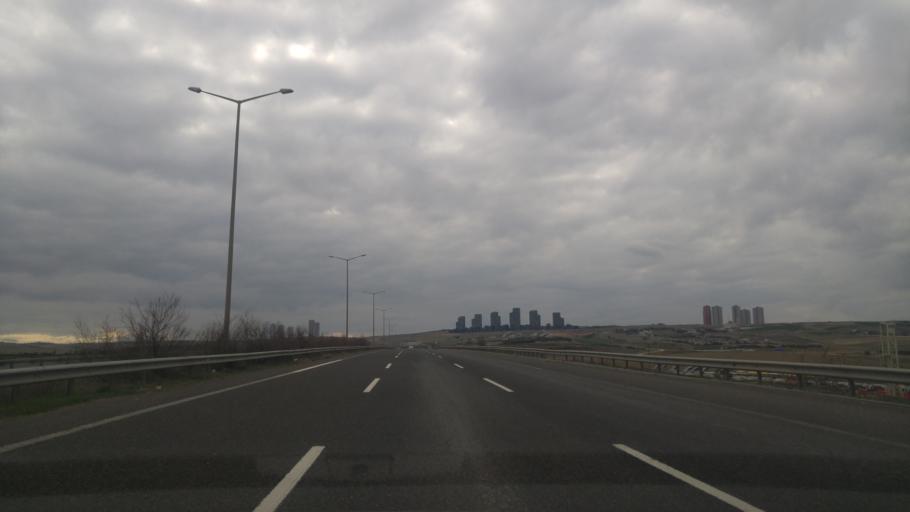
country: TR
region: Ankara
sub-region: Goelbasi
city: Golbasi
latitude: 39.7874
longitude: 32.7480
